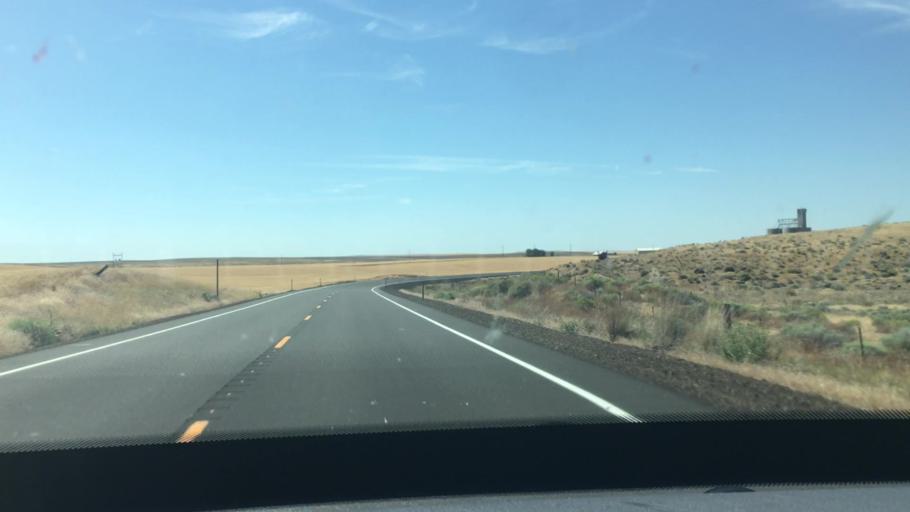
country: US
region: Oregon
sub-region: Sherman County
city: Moro
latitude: 45.3457
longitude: -120.7818
